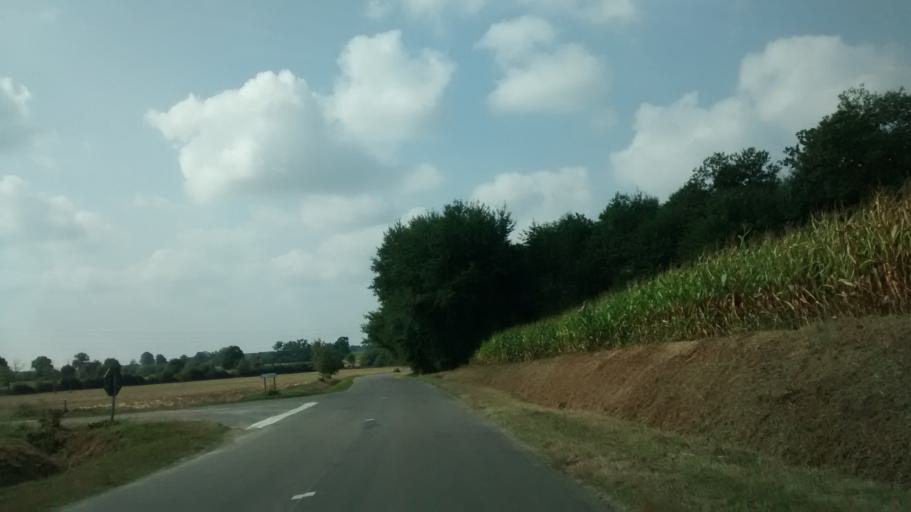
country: FR
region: Brittany
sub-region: Departement d'Ille-et-Vilaine
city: Chatillon-en-Vendelais
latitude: 48.2273
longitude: -1.2072
